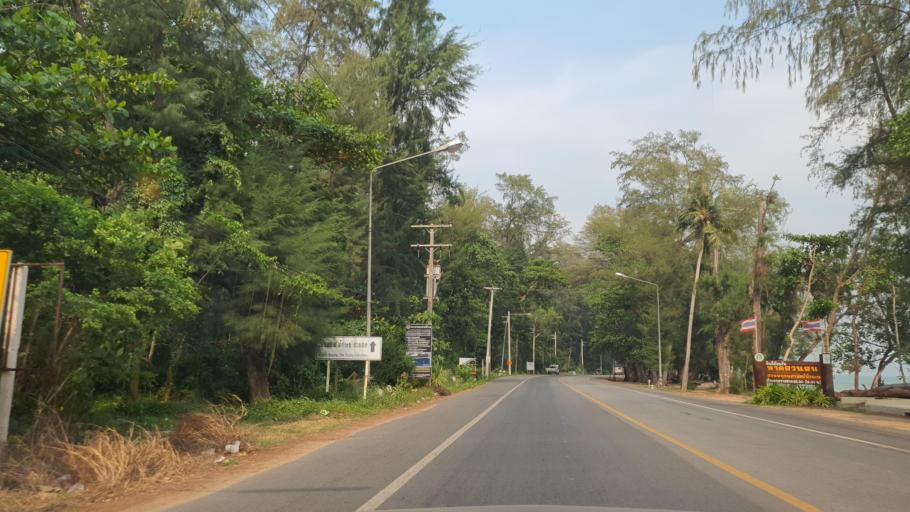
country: TH
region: Rayong
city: Rayong
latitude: 12.6317
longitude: 101.4518
